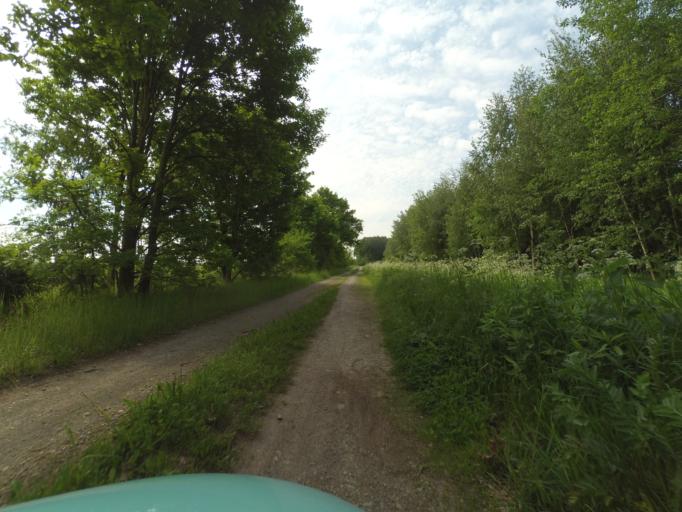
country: DE
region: Lower Saxony
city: Sehnde
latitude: 52.3360
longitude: 9.9665
